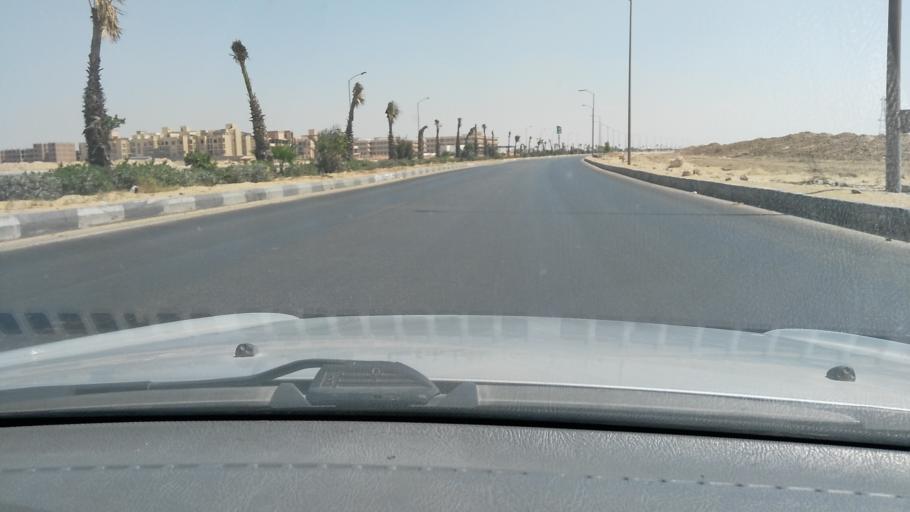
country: EG
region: Al Jizah
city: Madinat Sittah Uktubar
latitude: 29.9495
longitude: 30.9522
